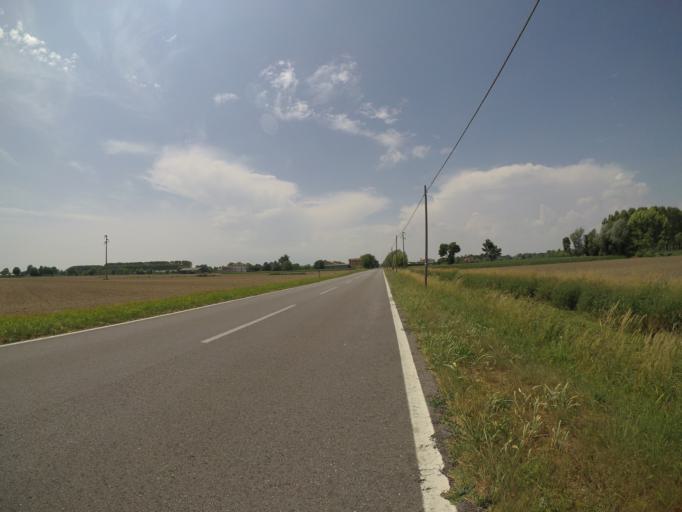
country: IT
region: Friuli Venezia Giulia
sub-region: Provincia di Udine
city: Teor
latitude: 45.8710
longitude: 13.0715
